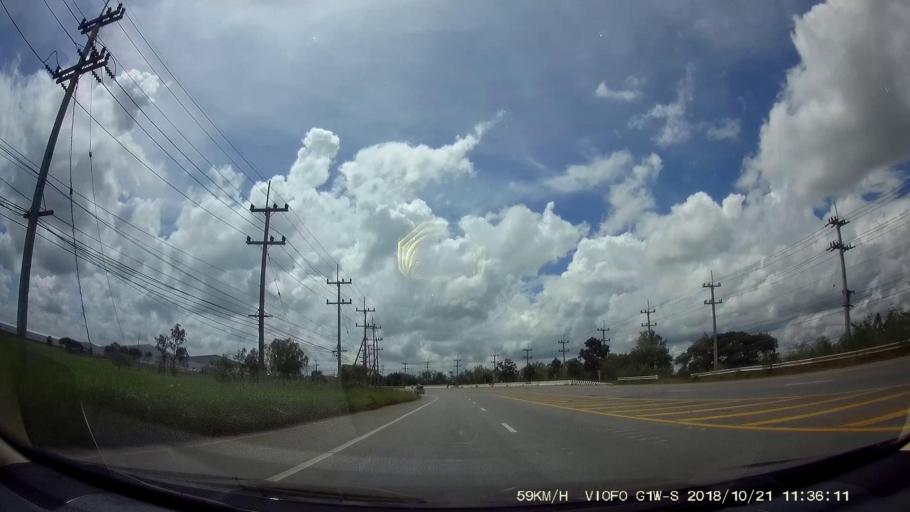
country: TH
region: Chaiyaphum
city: Chaiyaphum
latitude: 15.7217
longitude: 102.0169
